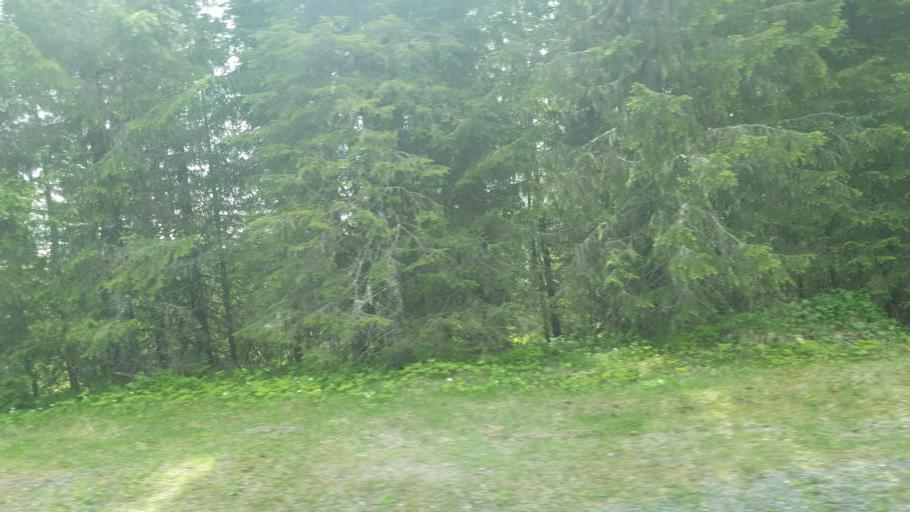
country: NO
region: Nord-Trondelag
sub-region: Leksvik
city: Leksvik
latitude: 63.6917
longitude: 10.4577
